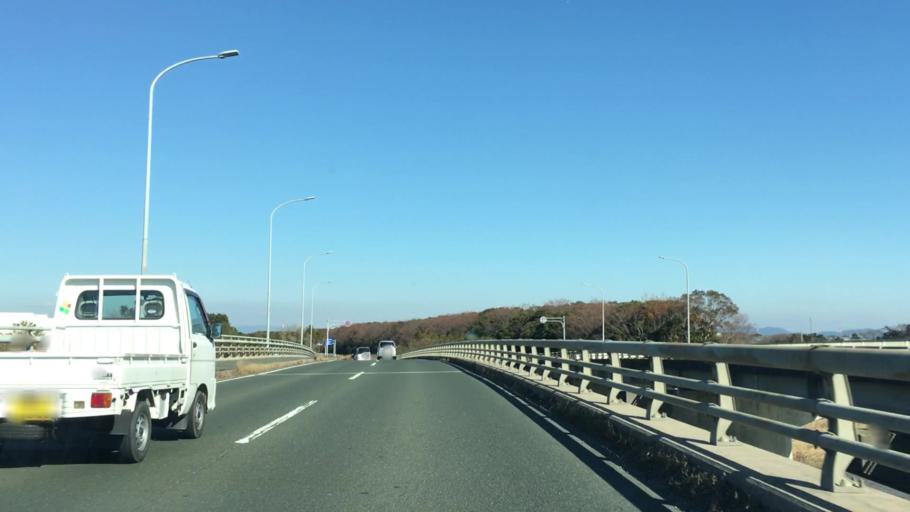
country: JP
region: Aichi
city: Tahara
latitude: 34.6938
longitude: 137.3225
